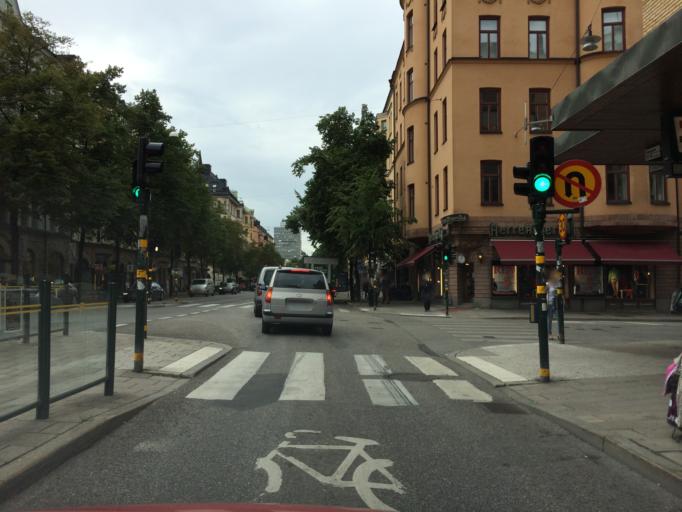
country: SE
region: Stockholm
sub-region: Stockholms Kommun
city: Stockholm
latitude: 59.3451
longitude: 18.0599
